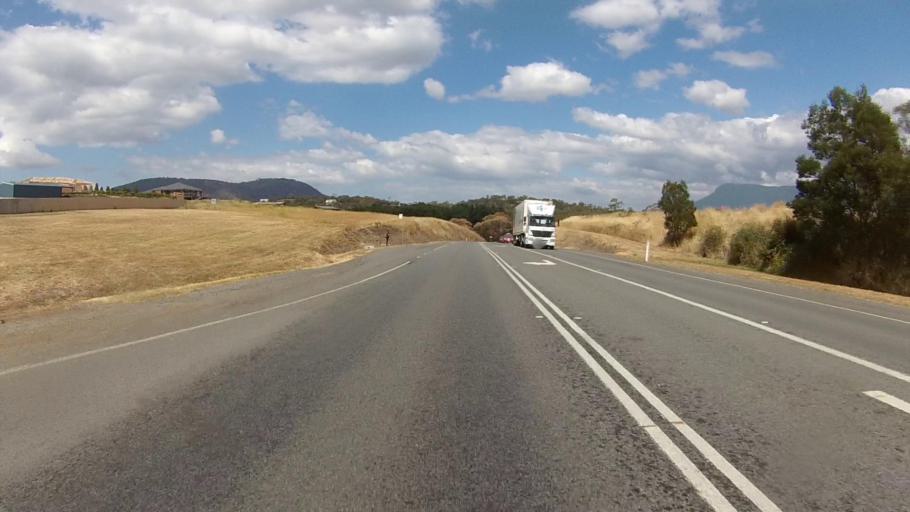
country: AU
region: Tasmania
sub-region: Brighton
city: Old Beach
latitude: -42.7625
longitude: 147.2691
